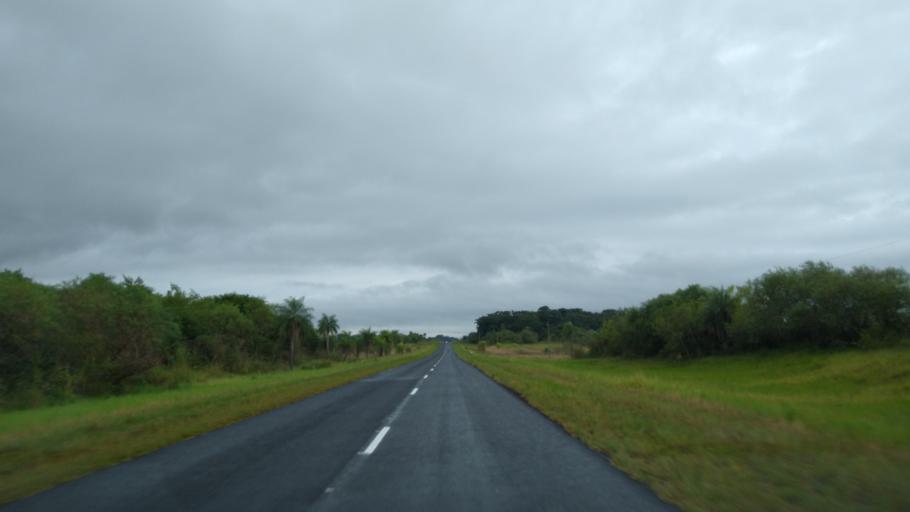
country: AR
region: Corrientes
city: Loreto
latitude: -27.7049
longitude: -57.2264
